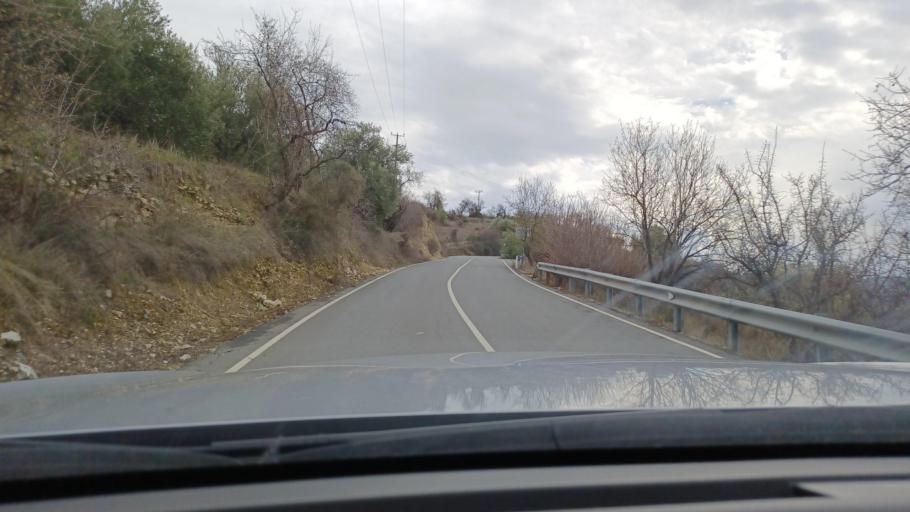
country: CY
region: Limassol
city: Pelendri
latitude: 34.8054
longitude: 32.9157
